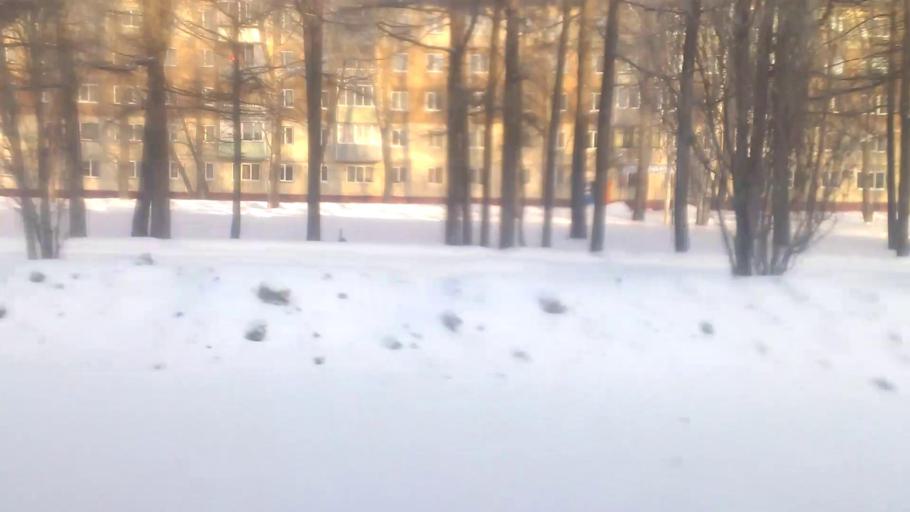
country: RU
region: Altai Krai
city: Novosilikatnyy
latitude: 53.3746
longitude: 83.6668
